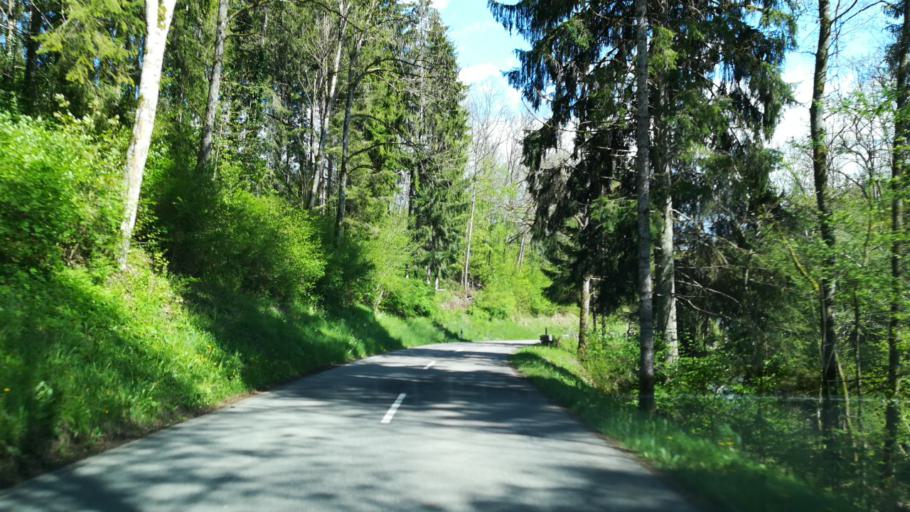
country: DE
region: Baden-Wuerttemberg
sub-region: Freiburg Region
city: Blumberg
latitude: 47.8457
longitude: 8.4615
